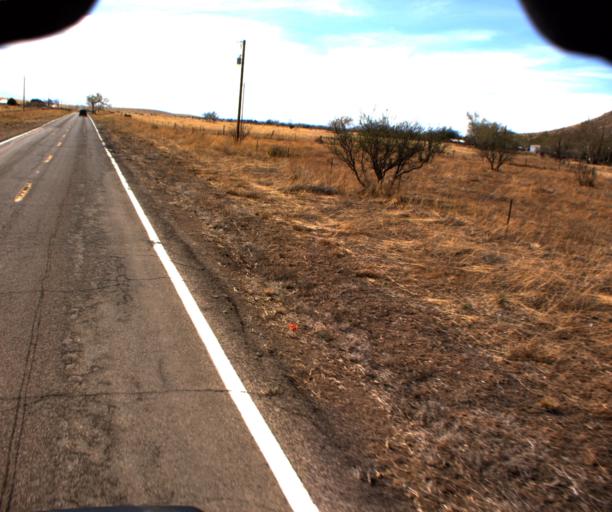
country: US
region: Arizona
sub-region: Cochise County
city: Willcox
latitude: 32.0067
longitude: -109.4001
